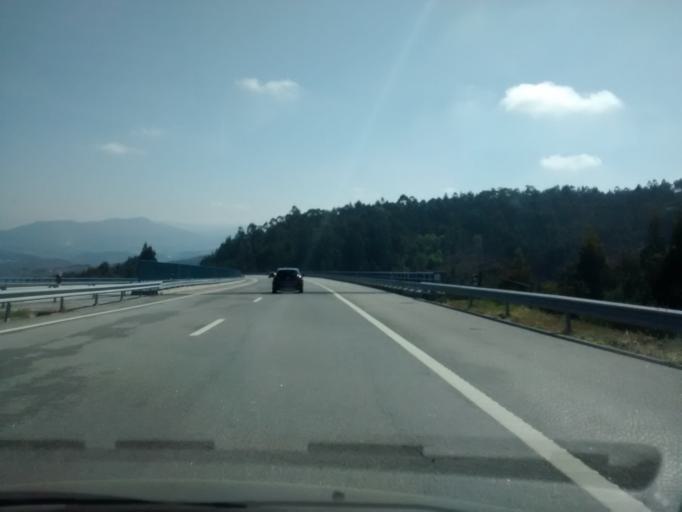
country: PT
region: Braga
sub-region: Cabeceiras de Basto
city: Refojos de Basto
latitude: 41.4710
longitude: -7.9897
